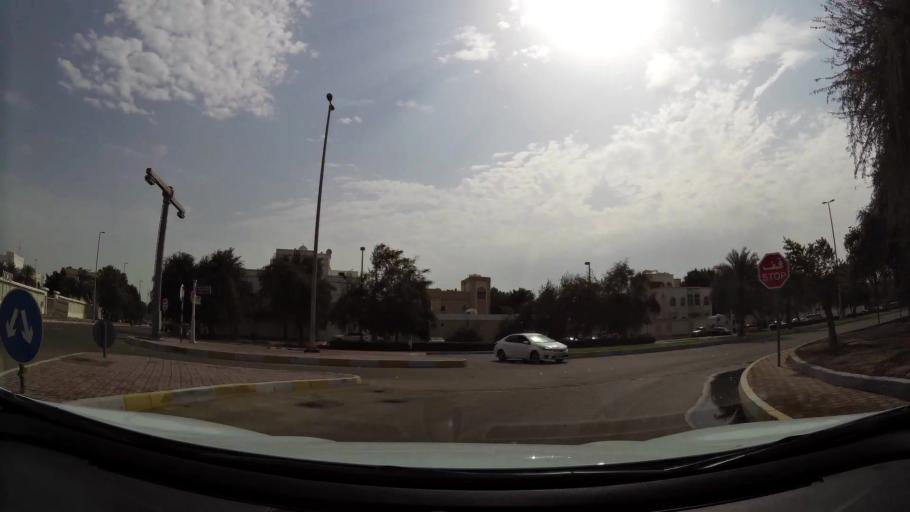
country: AE
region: Abu Dhabi
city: Abu Dhabi
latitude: 24.4429
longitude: 54.4280
